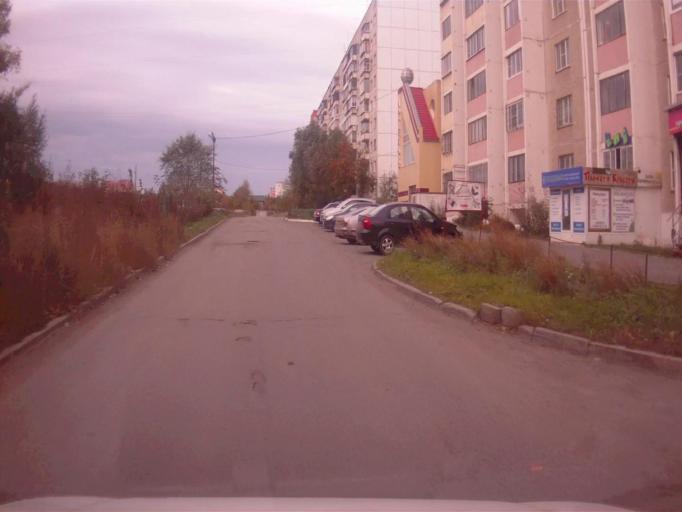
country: RU
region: Chelyabinsk
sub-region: Gorod Chelyabinsk
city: Chelyabinsk
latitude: 55.1795
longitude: 61.3218
